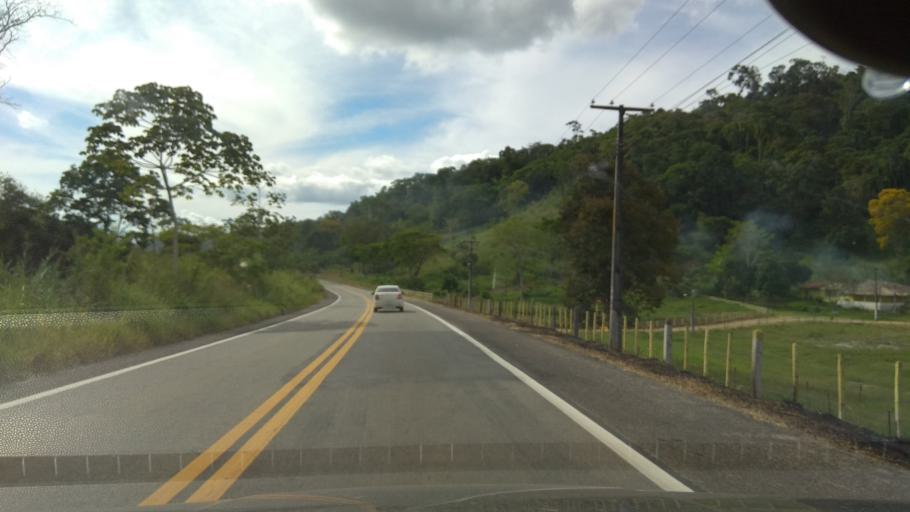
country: BR
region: Bahia
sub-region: Ipiau
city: Ipiau
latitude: -14.0822
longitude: -39.7811
